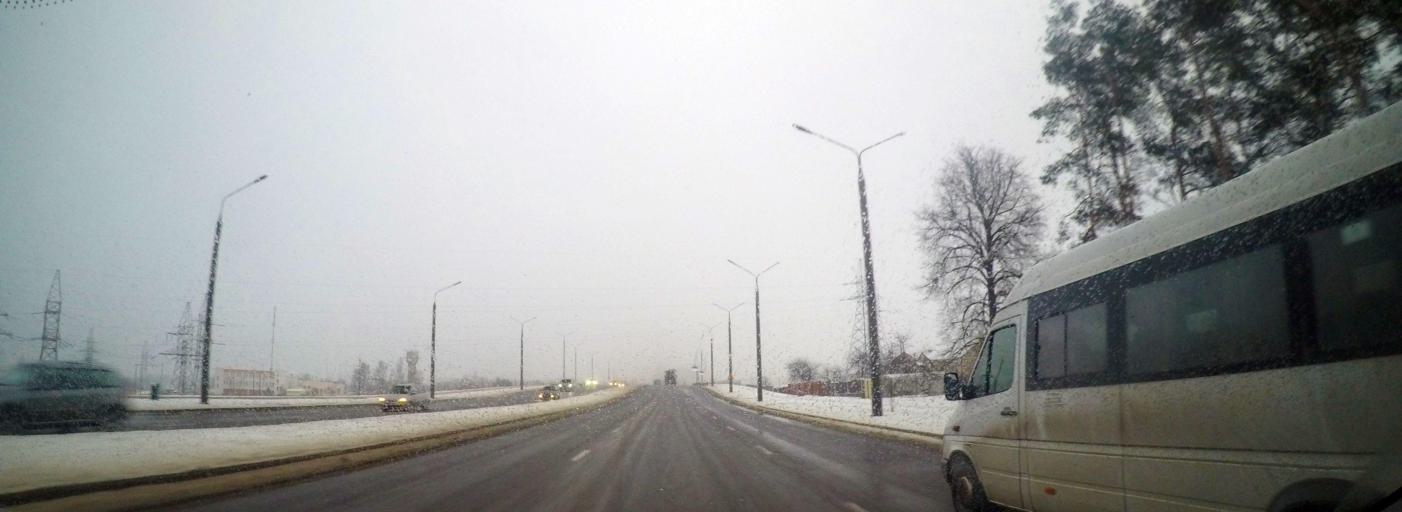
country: BY
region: Grodnenskaya
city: Hrodna
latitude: 53.6336
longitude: 23.8079
